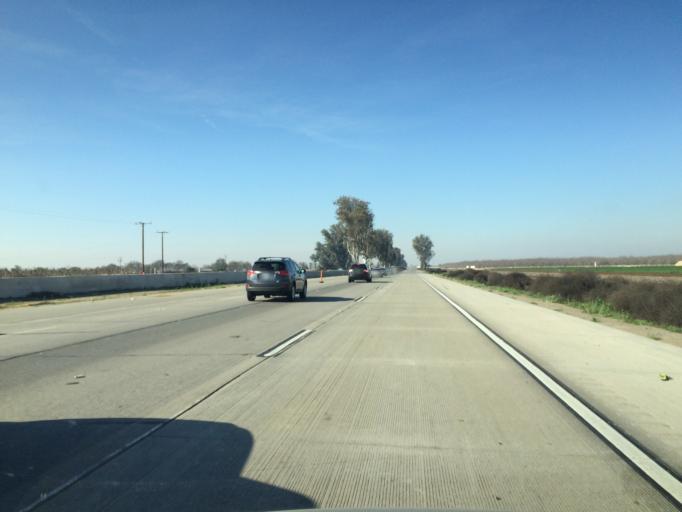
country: US
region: California
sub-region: Tulare County
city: Goshen
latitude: 36.3666
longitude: -119.4313
